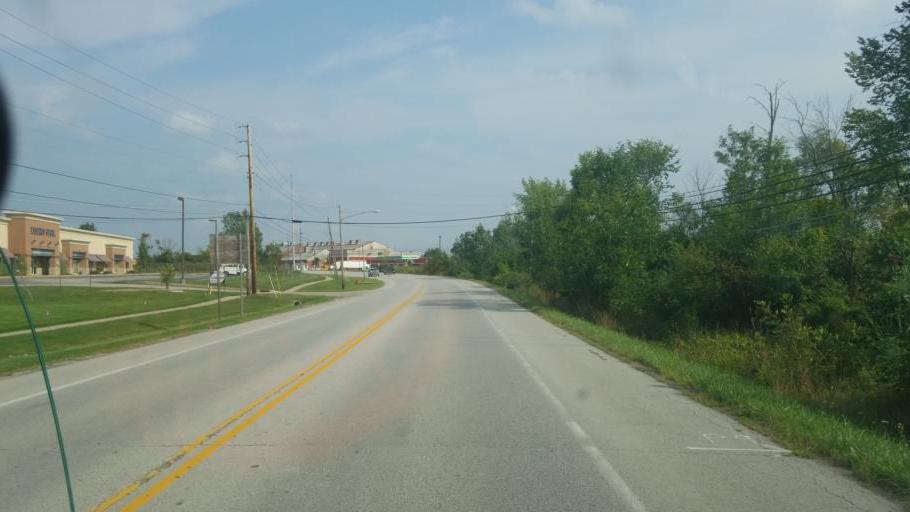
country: US
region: Ohio
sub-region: Medina County
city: Medina
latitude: 41.1406
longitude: -81.8845
